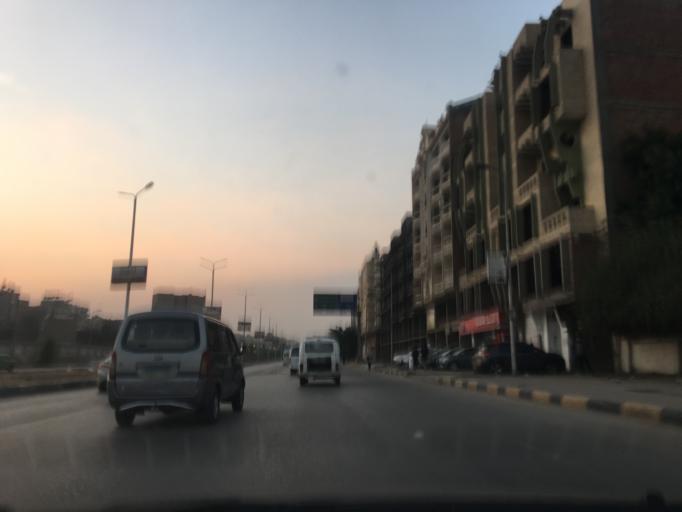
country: EG
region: Al Jizah
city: Al Jizah
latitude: 29.9893
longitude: 31.1376
